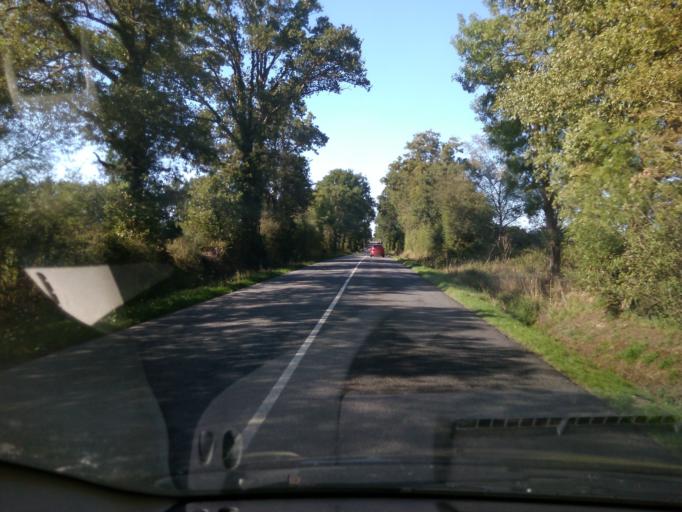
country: FR
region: Pays de la Loire
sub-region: Departement de la Loire-Atlantique
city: Quilly
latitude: 47.4359
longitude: -1.9257
